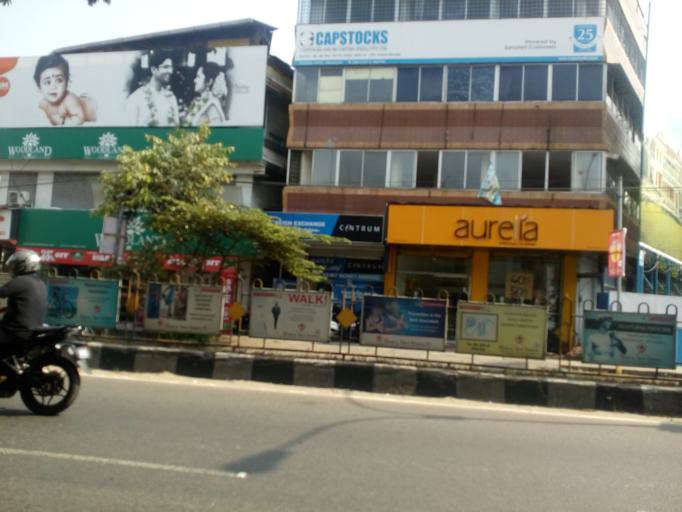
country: IN
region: Kerala
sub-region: Ernakulam
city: Cochin
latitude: 9.9654
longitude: 76.2866
